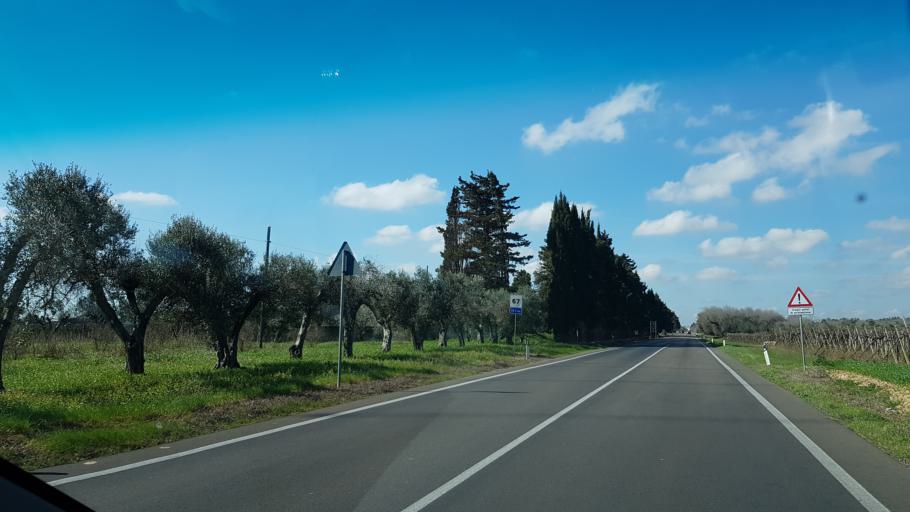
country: IT
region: Apulia
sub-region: Provincia di Lecce
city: Salice Salentino
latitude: 40.4001
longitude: 17.9815
